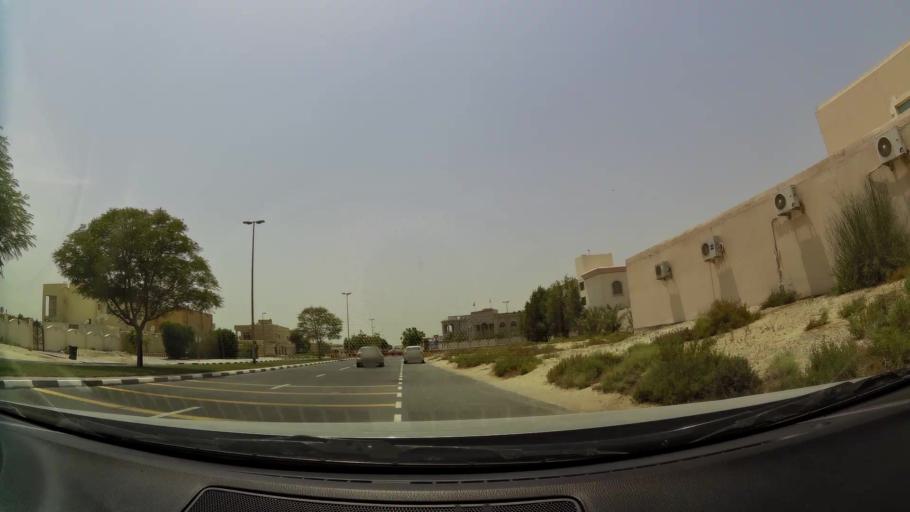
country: AE
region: Ash Shariqah
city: Sharjah
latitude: 25.2009
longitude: 55.3884
